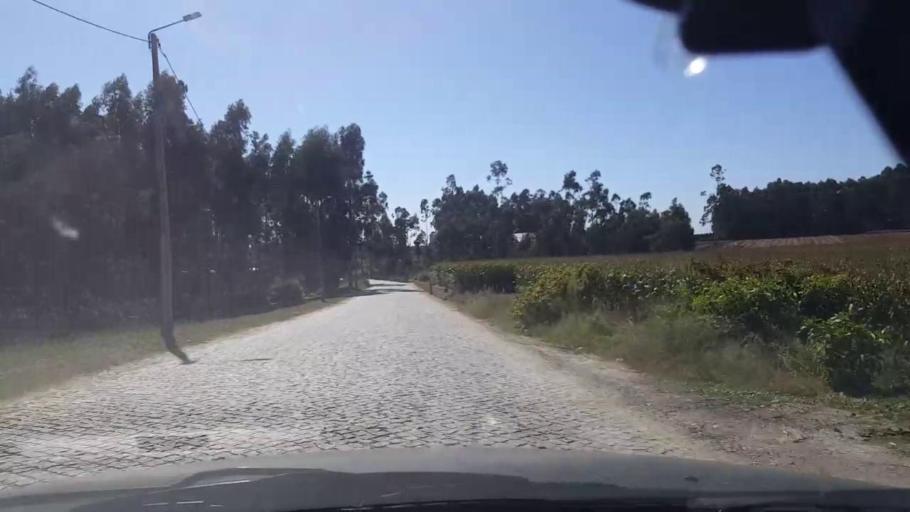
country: PT
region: Porto
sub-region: Matosinhos
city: Lavra
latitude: 41.2859
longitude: -8.6943
